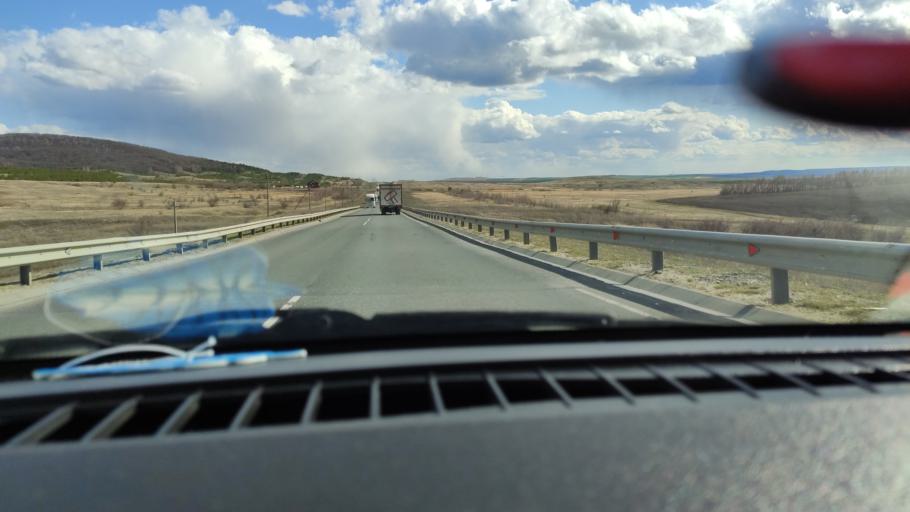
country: RU
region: Saratov
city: Alekseyevka
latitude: 52.3108
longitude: 47.9245
